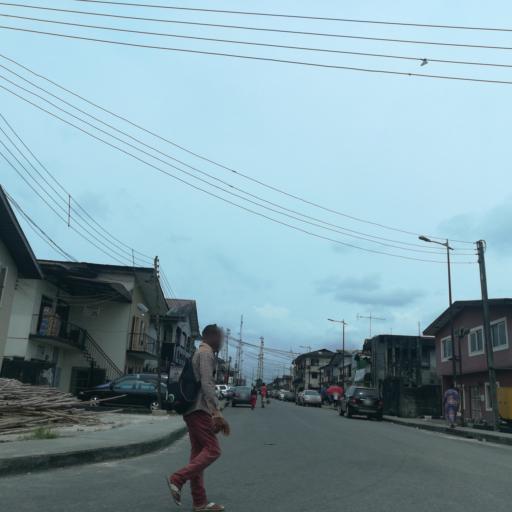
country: NG
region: Rivers
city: Port Harcourt
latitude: 4.7990
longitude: 7.0037
